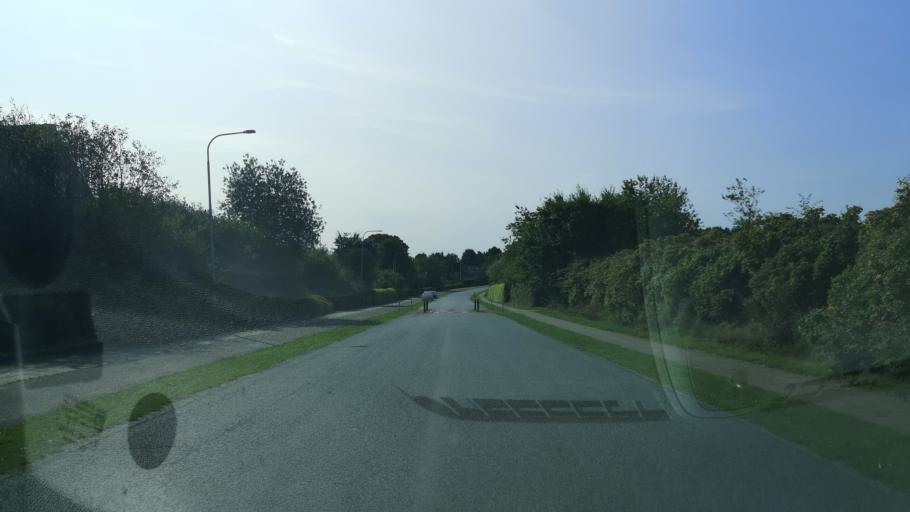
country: DK
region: Central Jutland
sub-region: Ringkobing-Skjern Kommune
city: Videbaek
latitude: 56.0842
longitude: 8.6221
